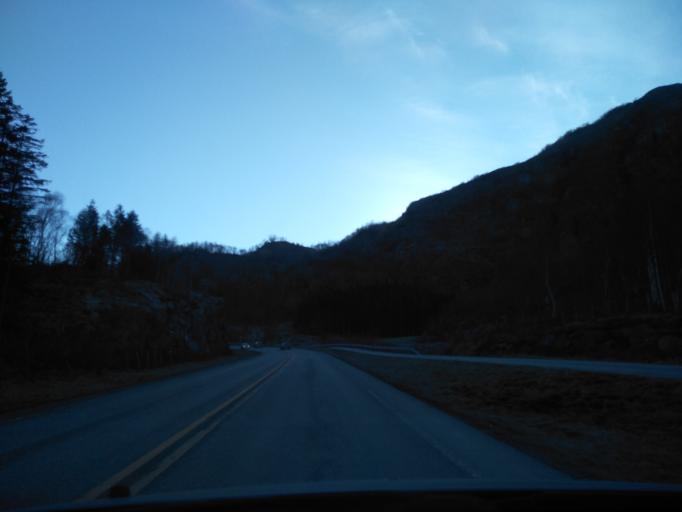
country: NO
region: Hordaland
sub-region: Etne
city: Etne
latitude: 59.7312
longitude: 6.1202
